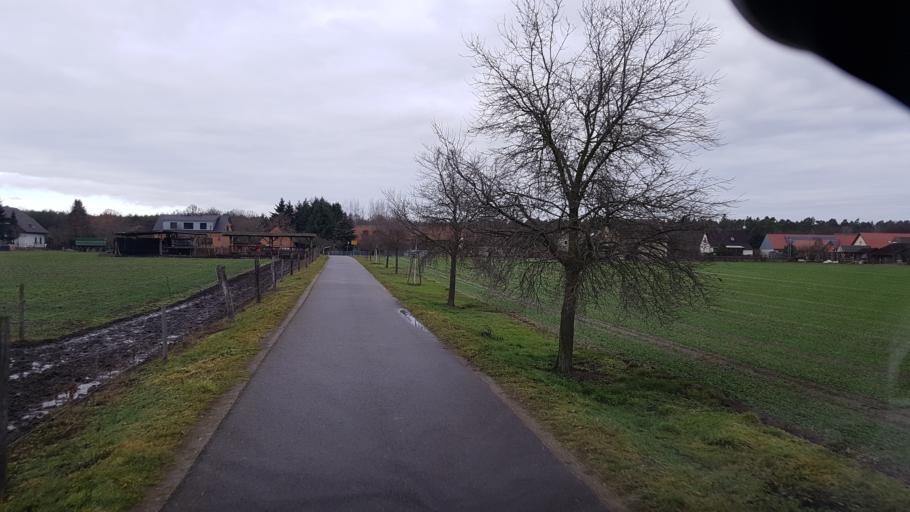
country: DE
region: Brandenburg
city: Altdobern
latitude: 51.6810
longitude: 14.0209
